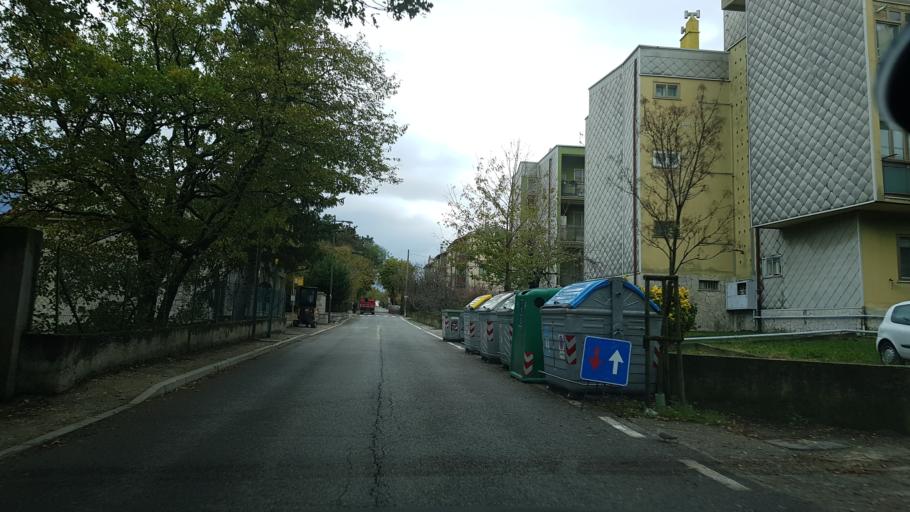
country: IT
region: Friuli Venezia Giulia
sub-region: Provincia di Trieste
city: Prosecco-Contovello
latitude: 45.7018
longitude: 13.7384
